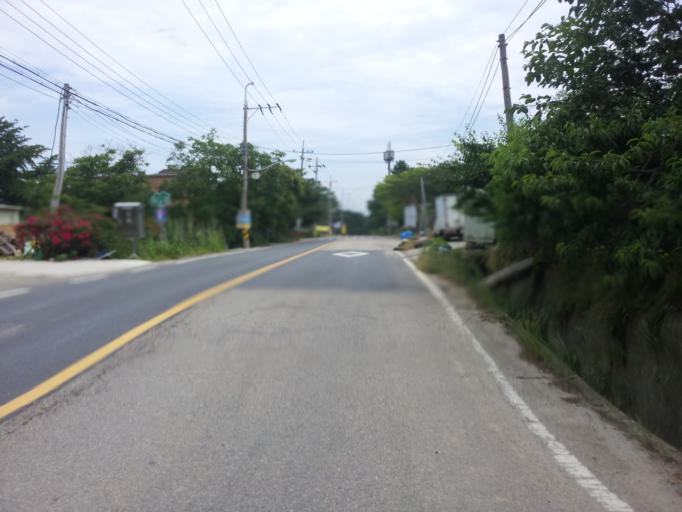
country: KR
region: Chungcheongbuk-do
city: Okcheon
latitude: 36.3652
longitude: 127.5028
